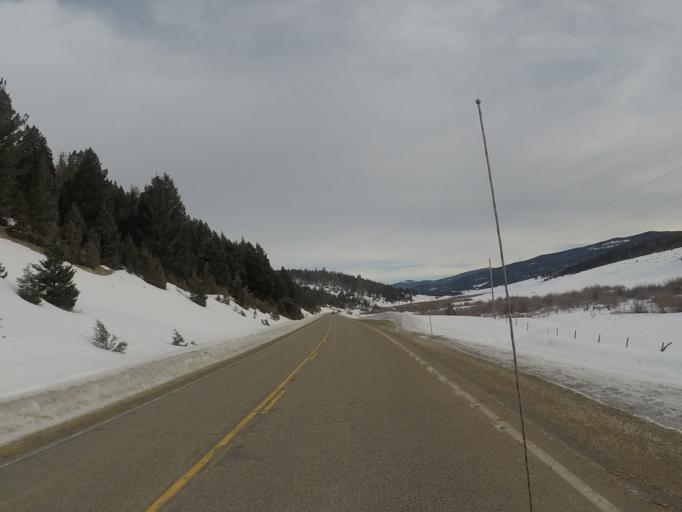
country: US
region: Montana
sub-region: Meagher County
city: White Sulphur Springs
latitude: 46.7003
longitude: -110.8625
